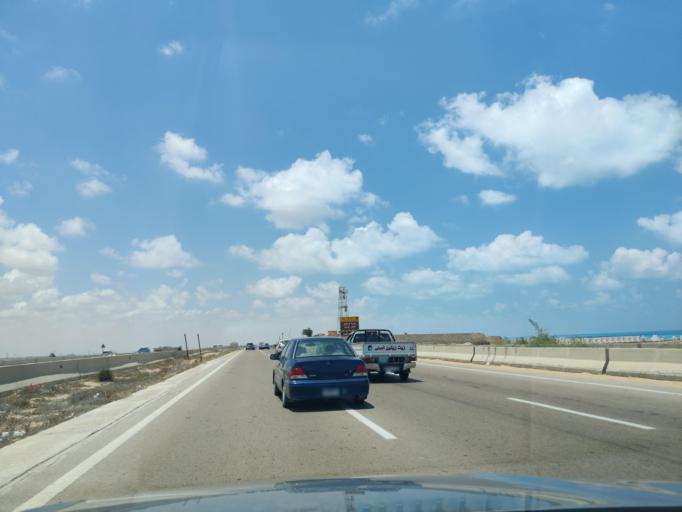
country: EG
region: Muhafazat Matruh
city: Al `Alamayn
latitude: 30.8273
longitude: 29.2021
